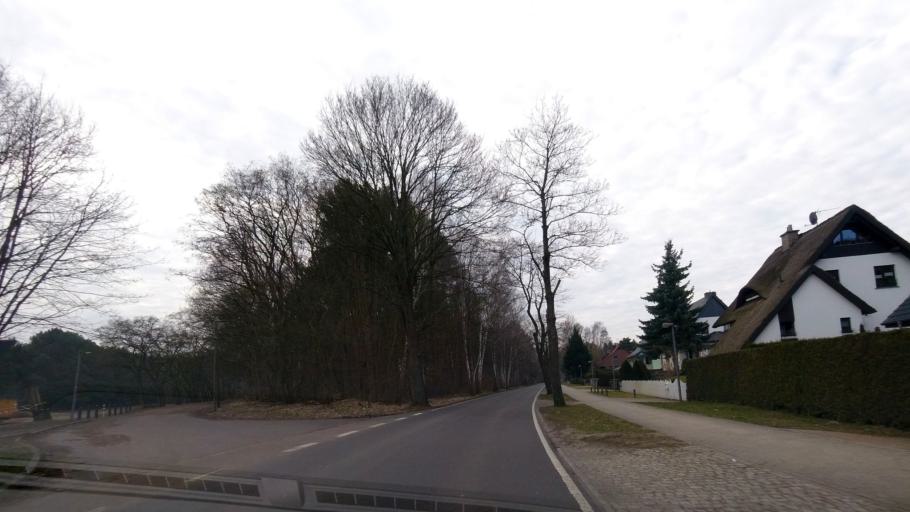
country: DE
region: Berlin
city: Schmockwitz
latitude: 52.3677
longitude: 13.7004
